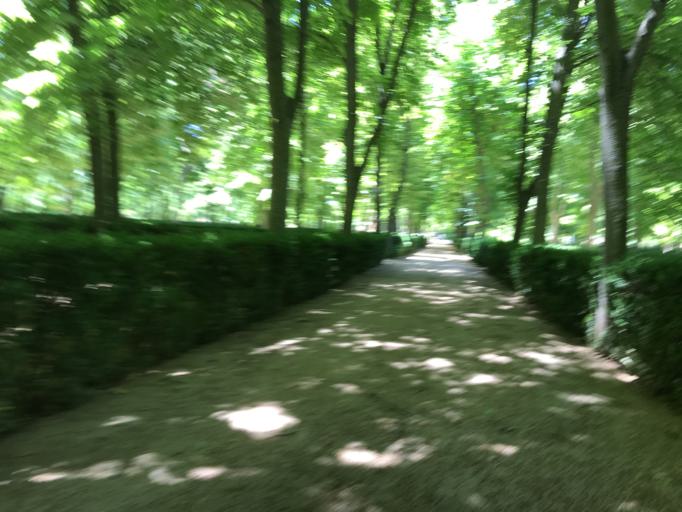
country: ES
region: Madrid
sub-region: Provincia de Madrid
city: Aranjuez
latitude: 40.0398
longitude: -3.6130
